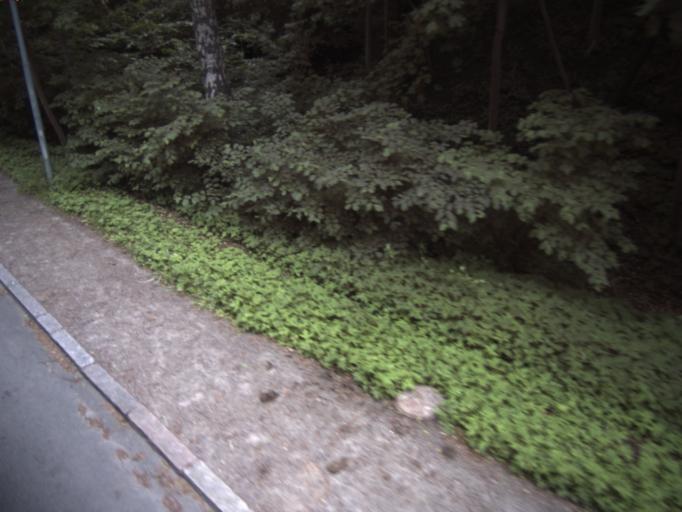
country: SE
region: Skane
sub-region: Helsingborg
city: Helsingborg
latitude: 56.0338
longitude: 12.7293
